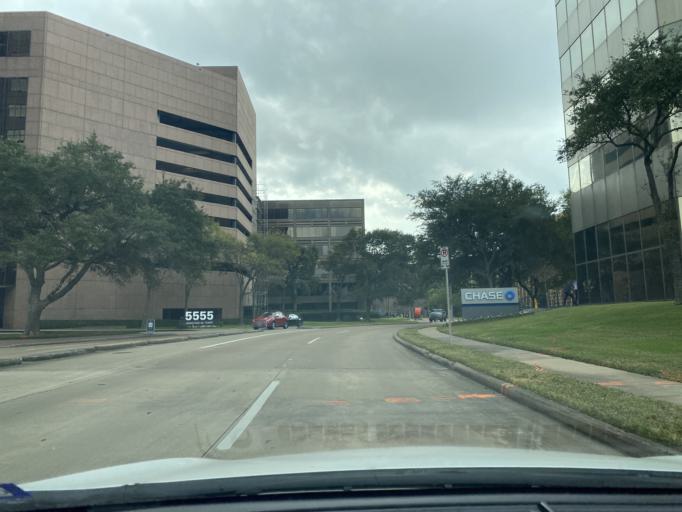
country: US
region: Texas
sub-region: Harris County
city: Hunters Creek Village
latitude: 29.7498
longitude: -95.4729
